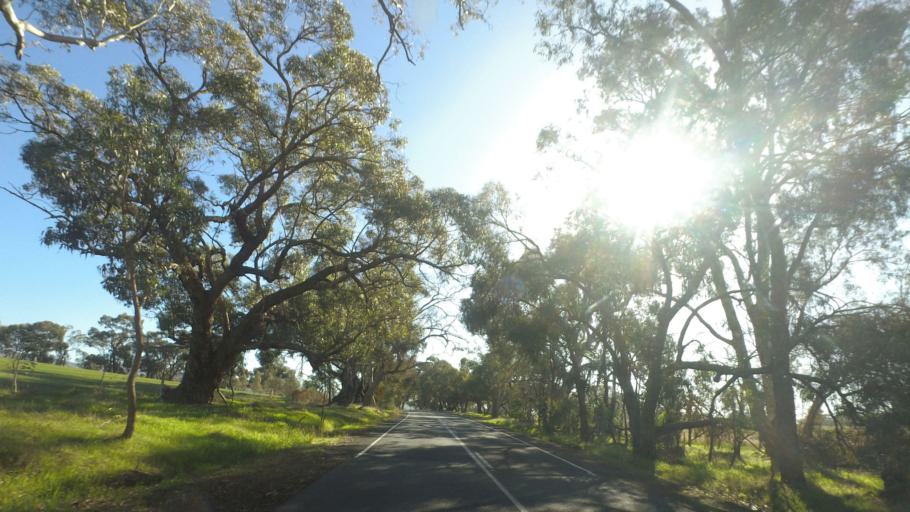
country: AU
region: Victoria
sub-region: Mount Alexander
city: Castlemaine
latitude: -36.9546
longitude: 144.3449
